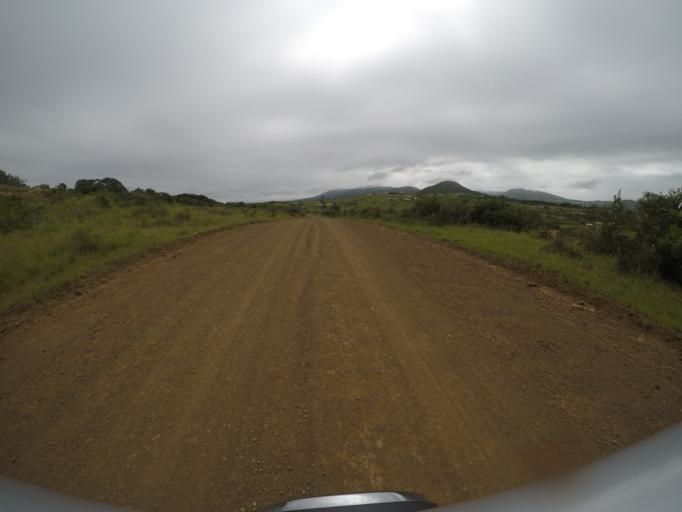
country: ZA
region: KwaZulu-Natal
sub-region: uThungulu District Municipality
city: Empangeni
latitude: -28.6060
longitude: 31.8363
